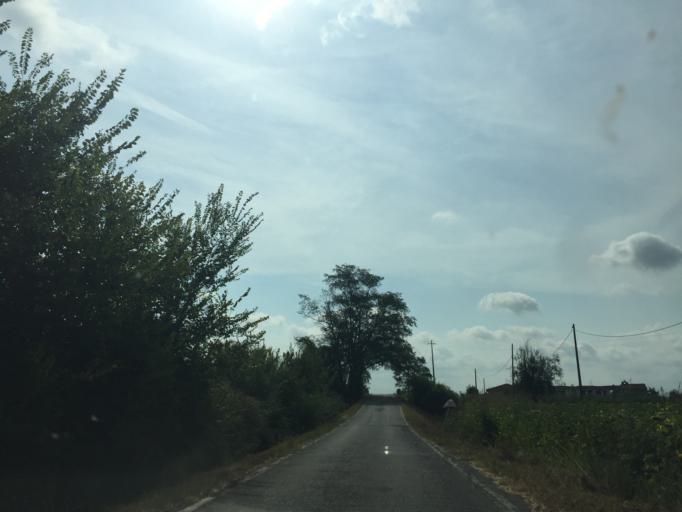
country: IT
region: Tuscany
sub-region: Provincia di Pistoia
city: Uggia-Pazzera-Bizzarrino
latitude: 43.8360
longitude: 10.8243
